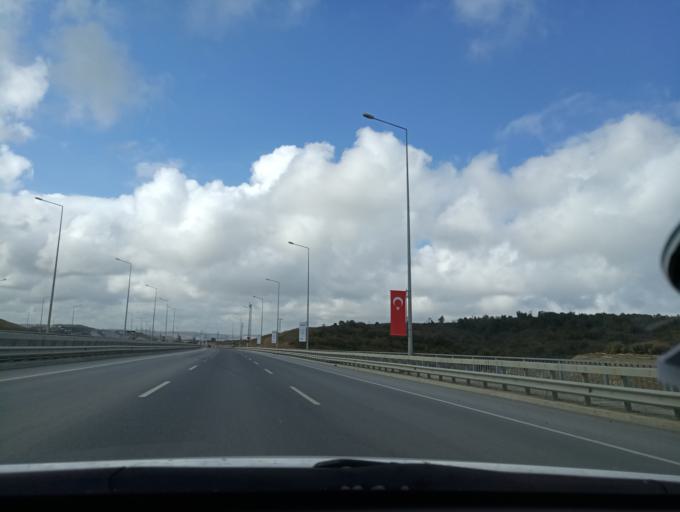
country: TR
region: Istanbul
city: Durusu
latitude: 41.2447
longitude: 28.7767
